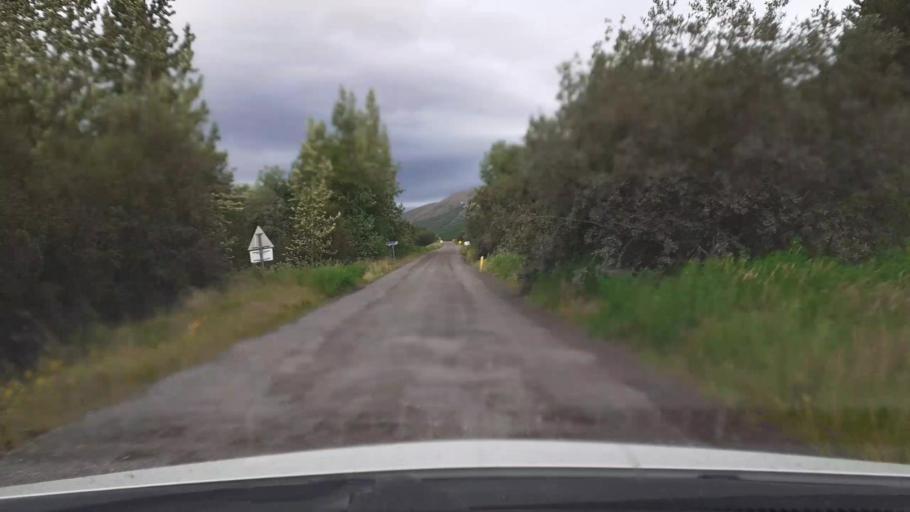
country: IS
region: Capital Region
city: Mosfellsbaer
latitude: 64.5301
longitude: -21.5100
